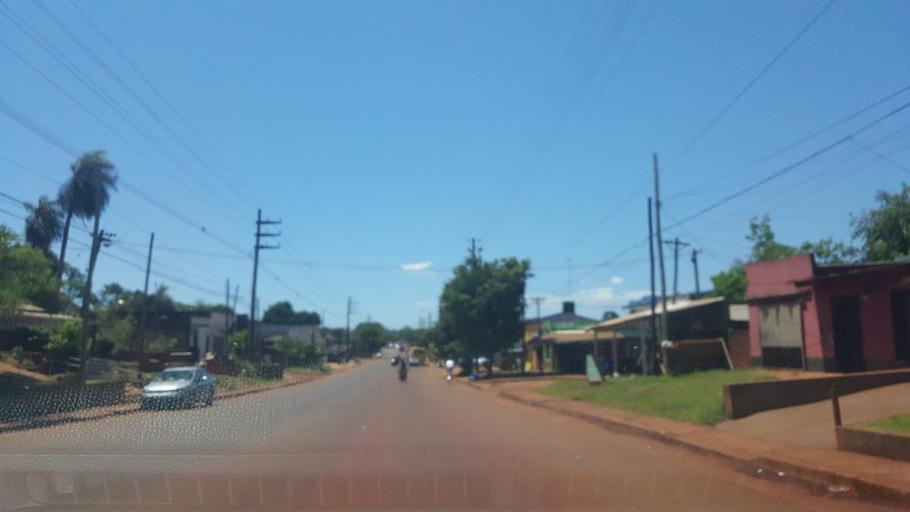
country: AR
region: Misiones
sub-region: Departamento de Capital
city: Posadas
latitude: -27.4131
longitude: -55.9122
